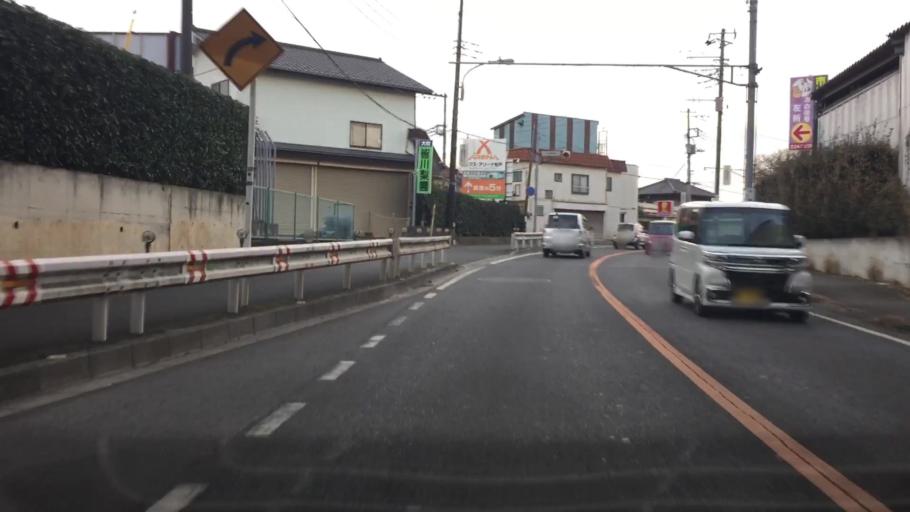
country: JP
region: Chiba
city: Matsudo
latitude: 35.7751
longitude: 139.9728
